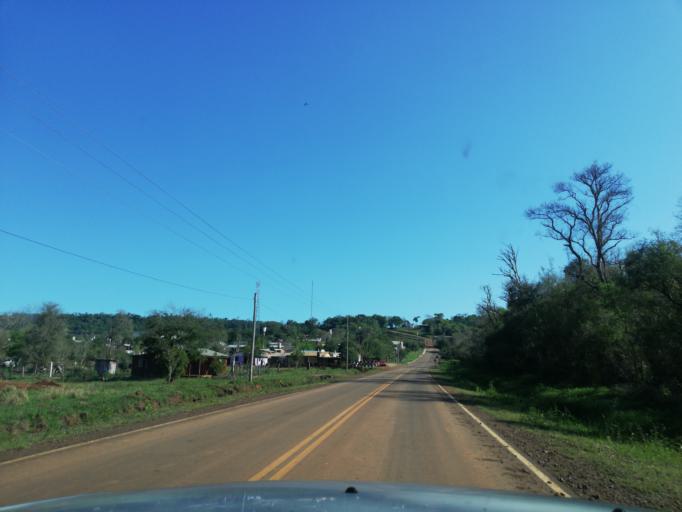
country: AR
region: Misiones
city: Arroyo del Medio
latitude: -27.6945
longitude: -55.4025
